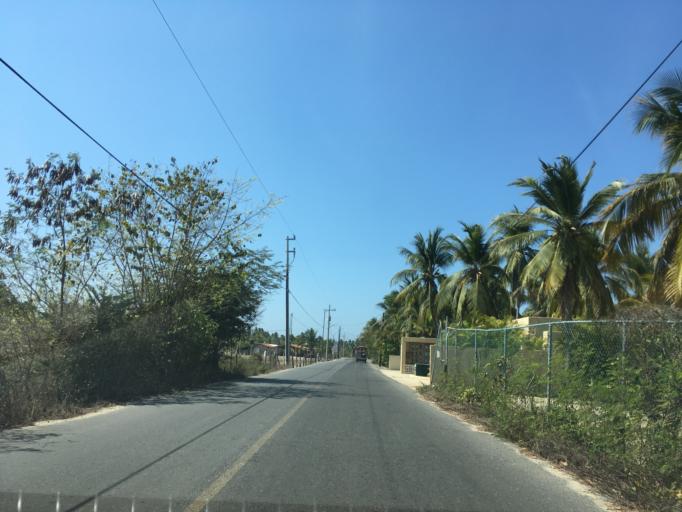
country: MX
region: Guerrero
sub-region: Zihuatanejo de Azueta
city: Los Achotes
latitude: 17.5454
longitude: -101.4388
